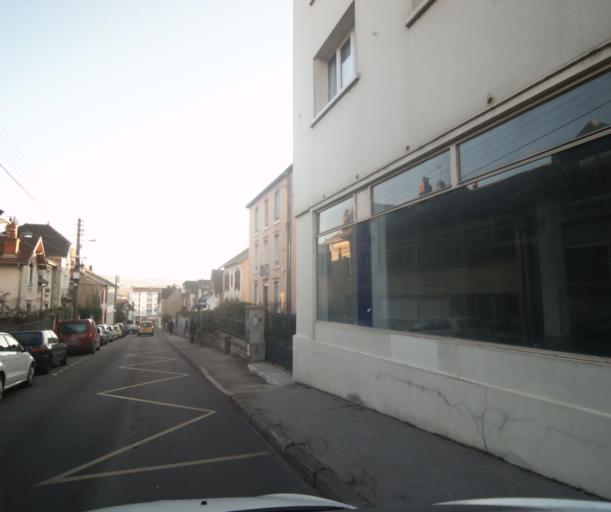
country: FR
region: Franche-Comte
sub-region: Departement du Doubs
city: Besancon
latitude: 47.2504
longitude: 6.0299
